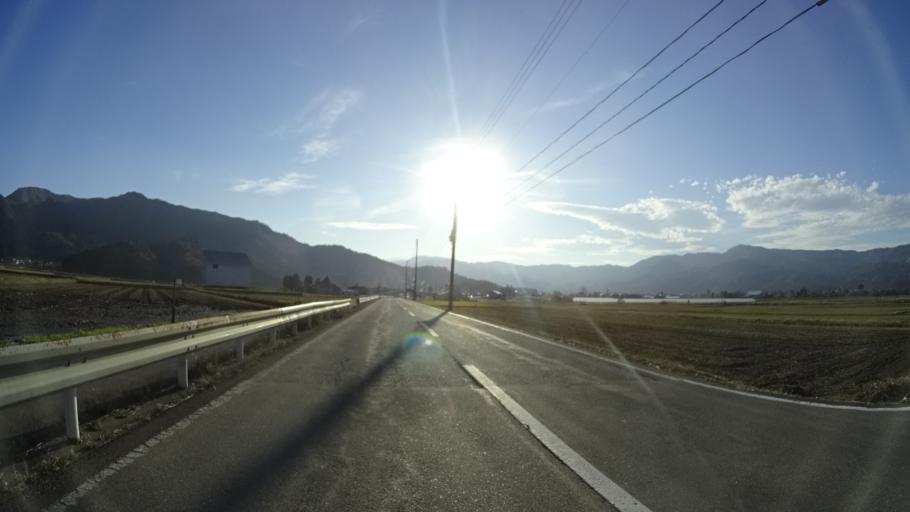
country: JP
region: Niigata
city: Shiozawa
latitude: 37.0136
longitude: 138.8549
